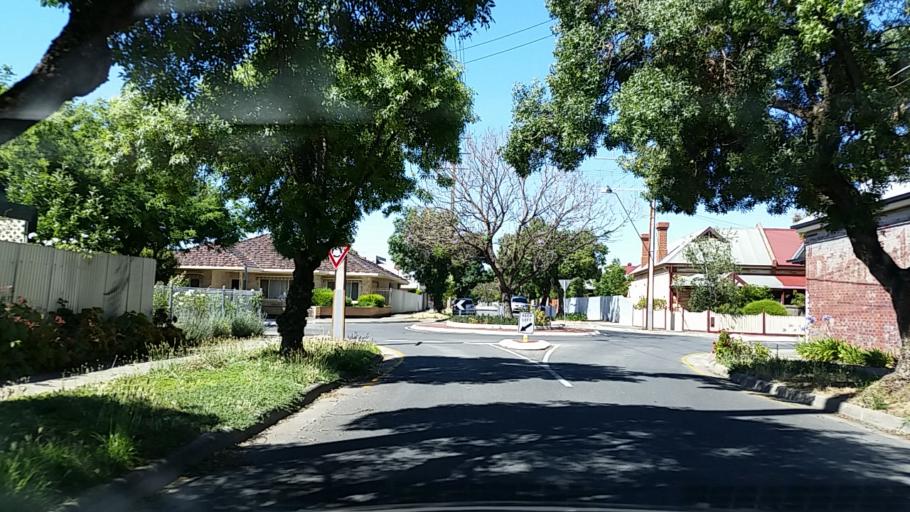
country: AU
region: South Australia
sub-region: Charles Sturt
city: Allenby Gardens
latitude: -34.8934
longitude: 138.5606
